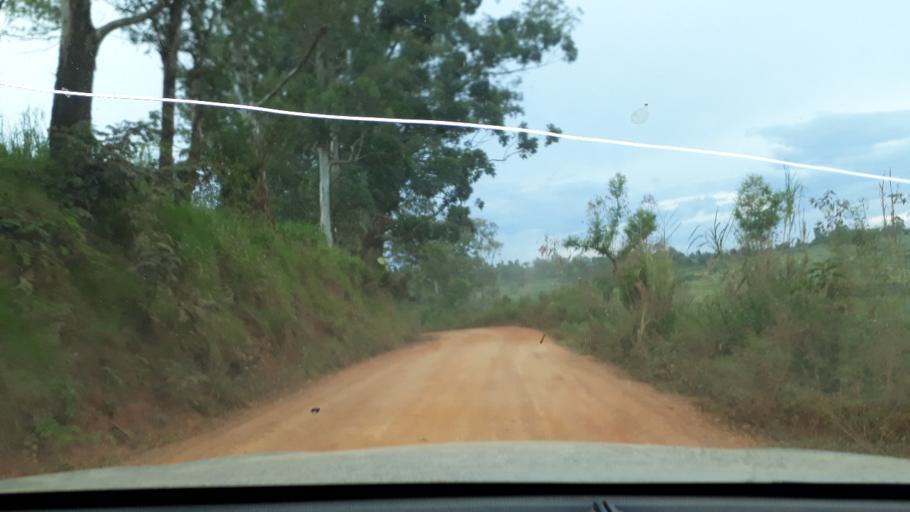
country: CD
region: Eastern Province
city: Bunia
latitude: 1.8701
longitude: 30.4814
